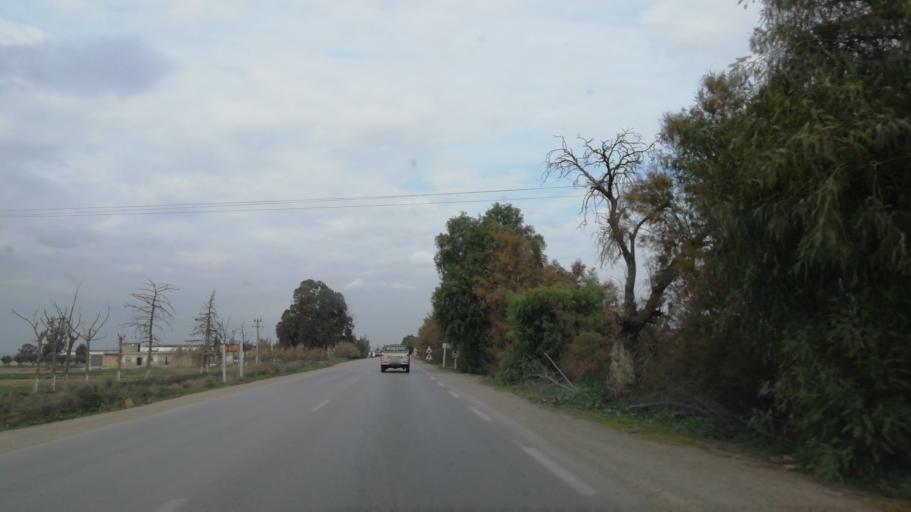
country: DZ
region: Mascara
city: Mascara
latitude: 35.6529
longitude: 0.0593
